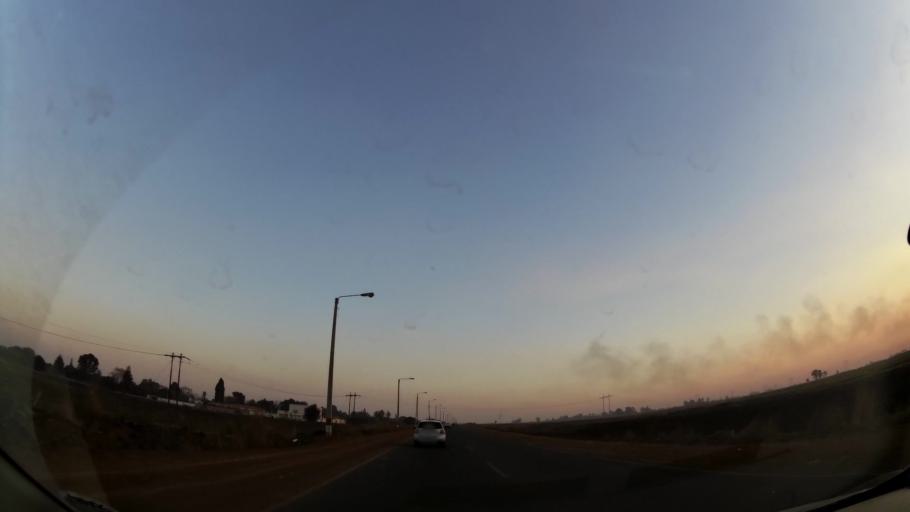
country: ZA
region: Gauteng
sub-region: Ekurhuleni Metropolitan Municipality
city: Springs
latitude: -26.3358
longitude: 28.4214
